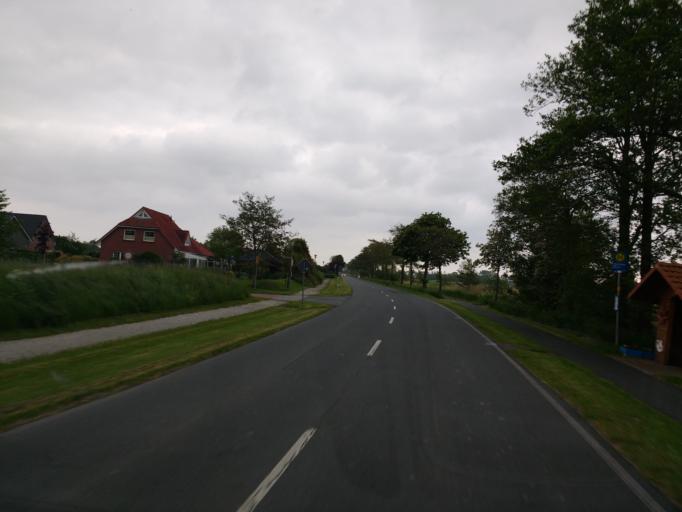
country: DE
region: Lower Saxony
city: Schillig
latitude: 53.6668
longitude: 7.9572
